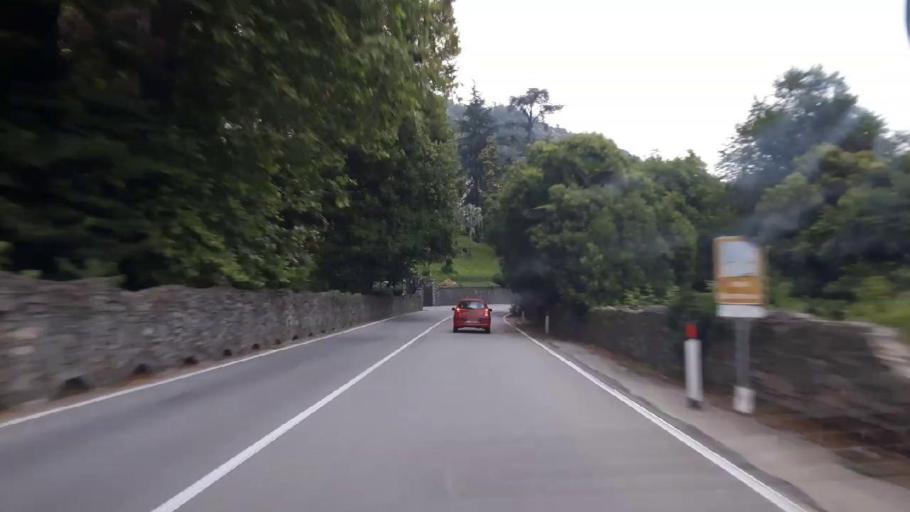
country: IT
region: Piedmont
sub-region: Provincia di Novara
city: Massino Visconti
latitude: 45.8100
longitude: 8.5435
